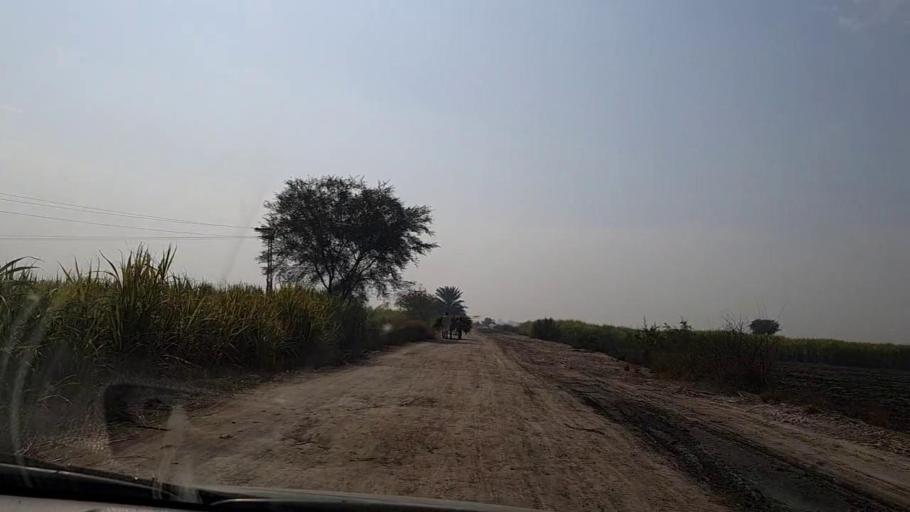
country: PK
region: Sindh
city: Daulatpur
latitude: 26.5509
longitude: 67.9819
